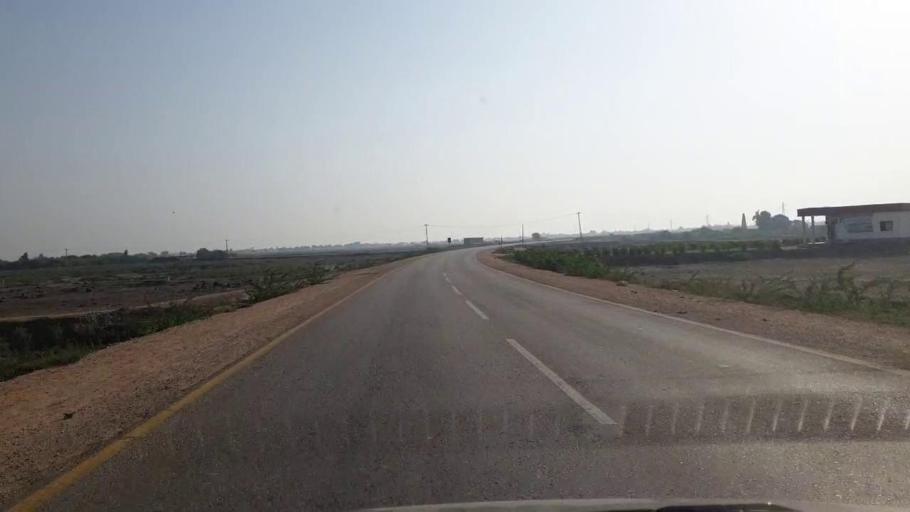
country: PK
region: Sindh
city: Badin
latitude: 24.6811
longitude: 68.8361
